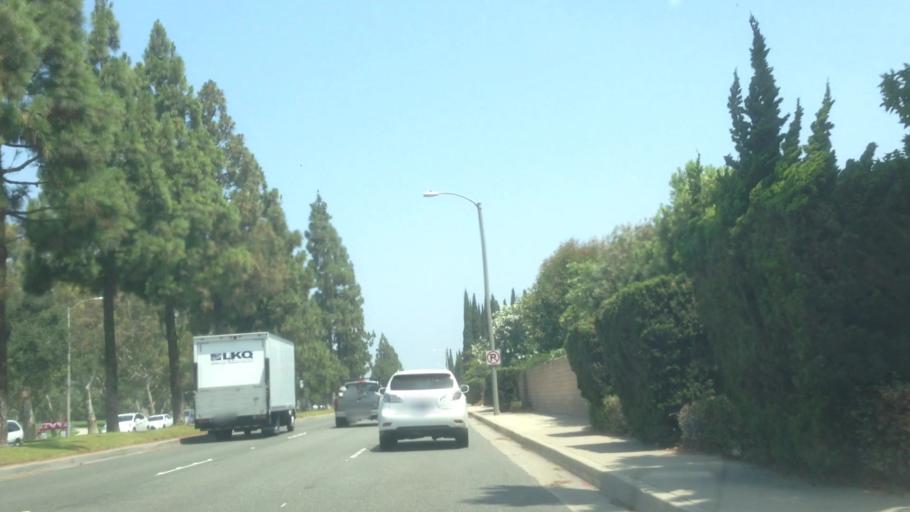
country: US
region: California
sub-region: Orange County
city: Fountain Valley
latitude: 33.7275
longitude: -117.9372
